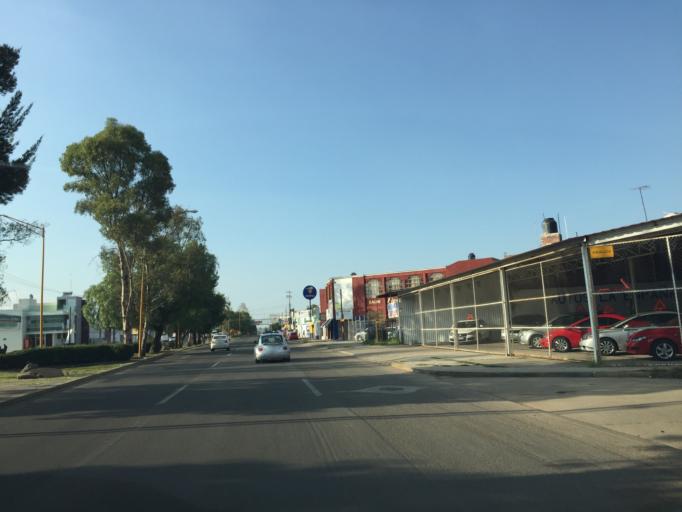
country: MX
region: Aguascalientes
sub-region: Aguascalientes
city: La Loma de los Negritos
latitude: 21.8617
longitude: -102.3170
